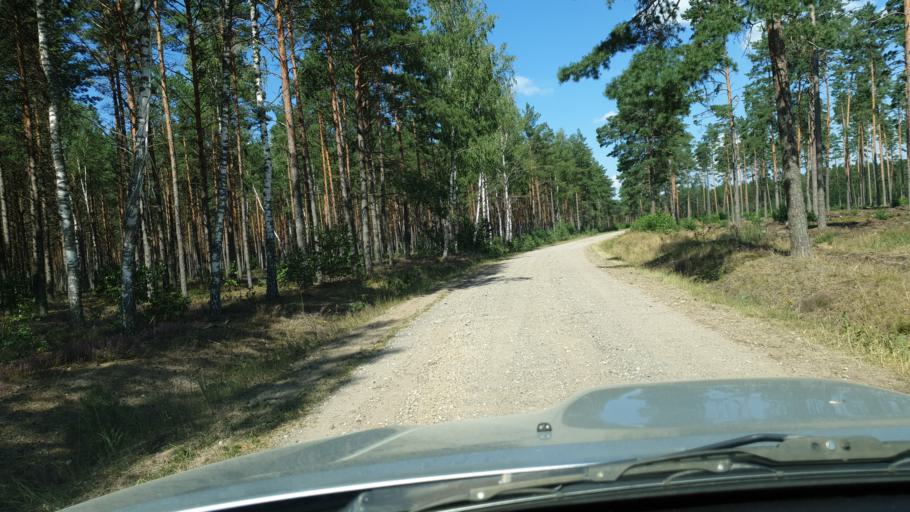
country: LT
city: Sirvintos
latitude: 54.8989
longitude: 24.9570
